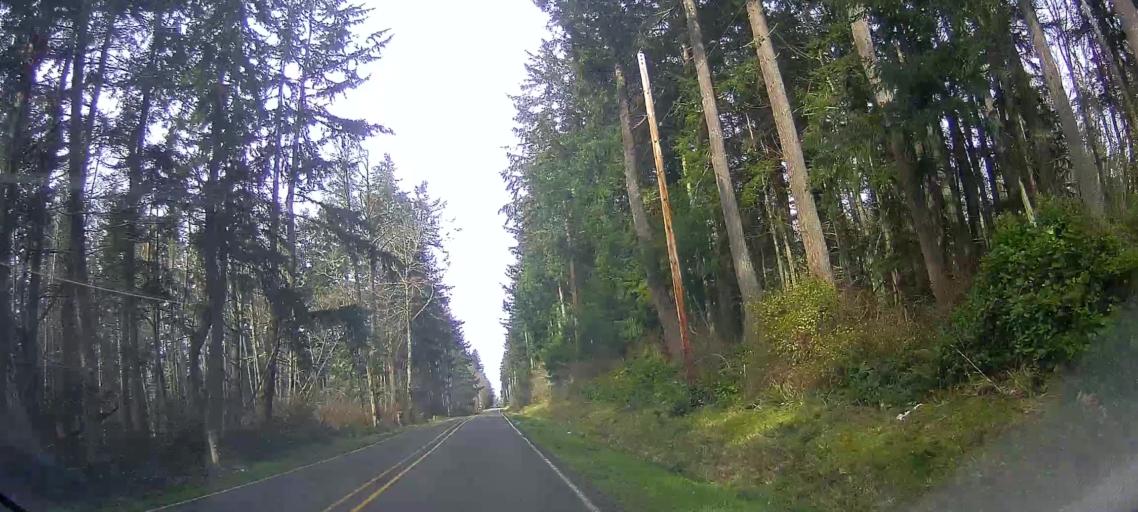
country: US
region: Washington
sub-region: Island County
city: Langley
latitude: 48.0701
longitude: -122.3701
